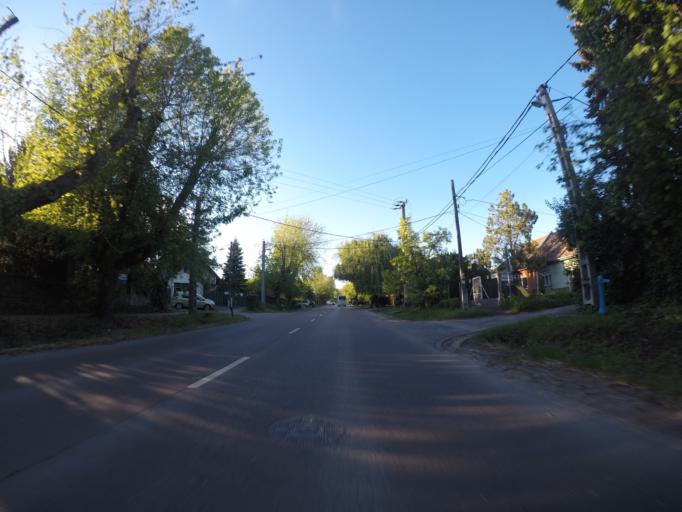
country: HU
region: Pest
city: Nagytarcsa
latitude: 47.4957
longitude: 19.2870
